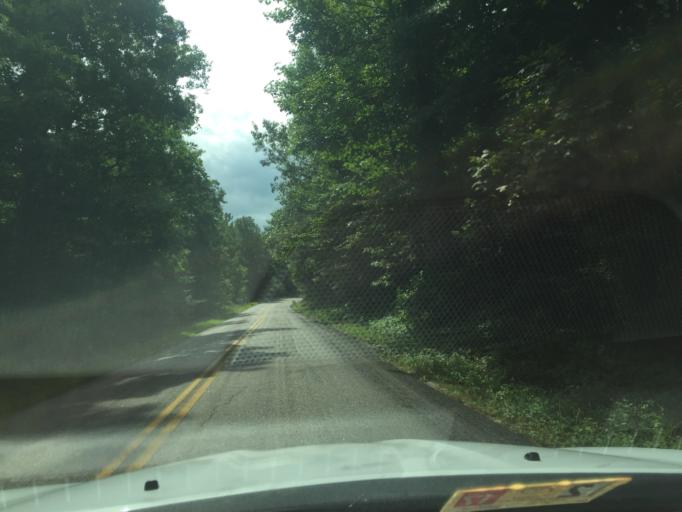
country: US
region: Virginia
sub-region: Charles City County
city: Charles City
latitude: 37.4101
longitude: -77.0293
